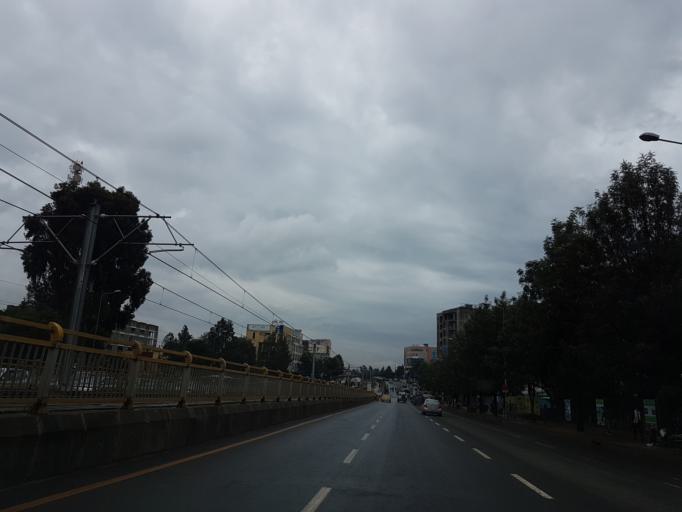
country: ET
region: Adis Abeba
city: Addis Ababa
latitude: 9.0192
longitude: 38.8183
